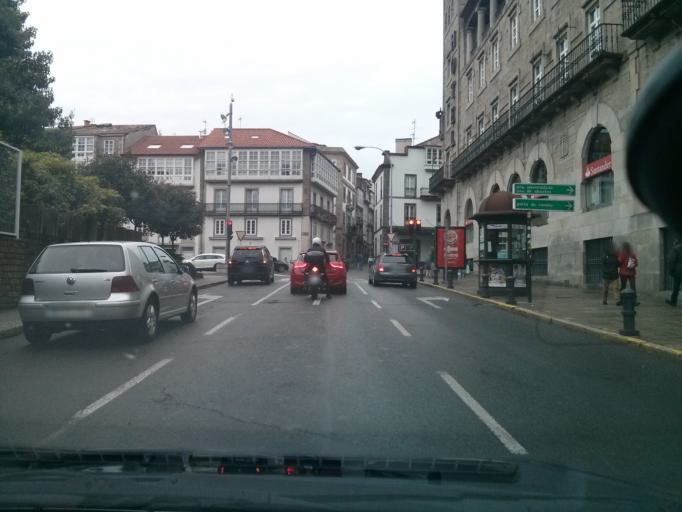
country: ES
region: Galicia
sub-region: Provincia da Coruna
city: Santiago de Compostela
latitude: 42.8763
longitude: -8.5441
